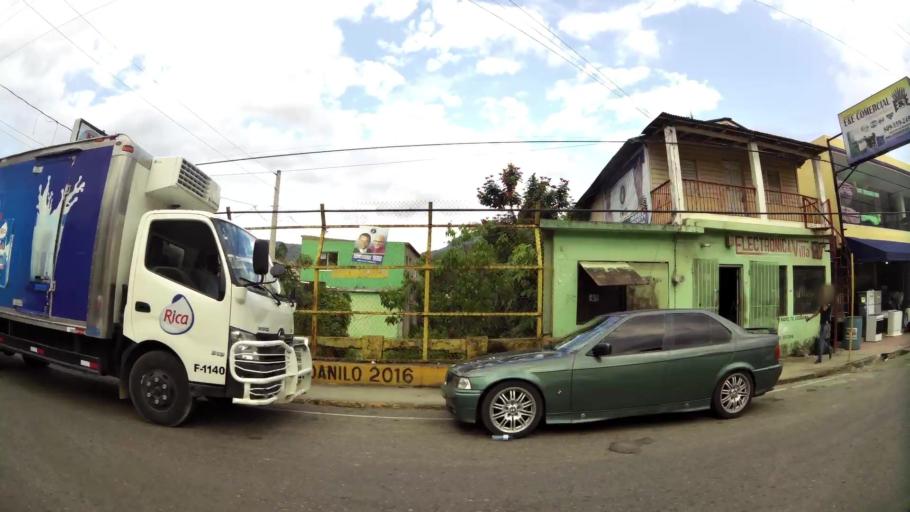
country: DO
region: San Cristobal
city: Villa Altagracia
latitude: 18.6754
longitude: -70.1755
